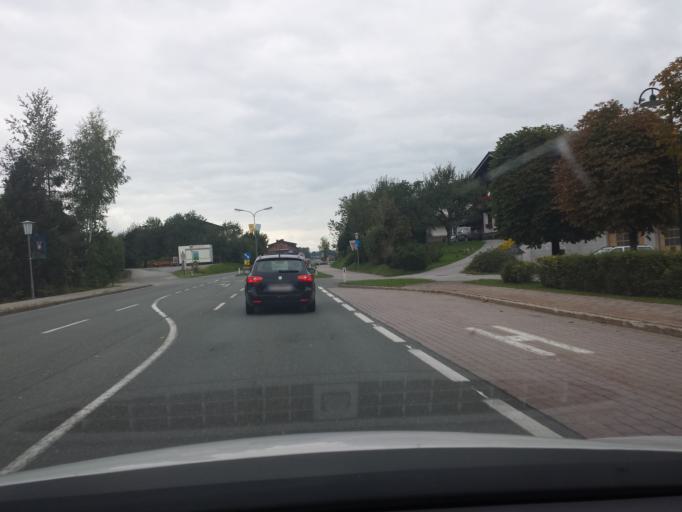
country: AT
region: Salzburg
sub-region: Politischer Bezirk Salzburg-Umgebung
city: Hof bei Salzburg
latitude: 47.8192
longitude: 13.2132
